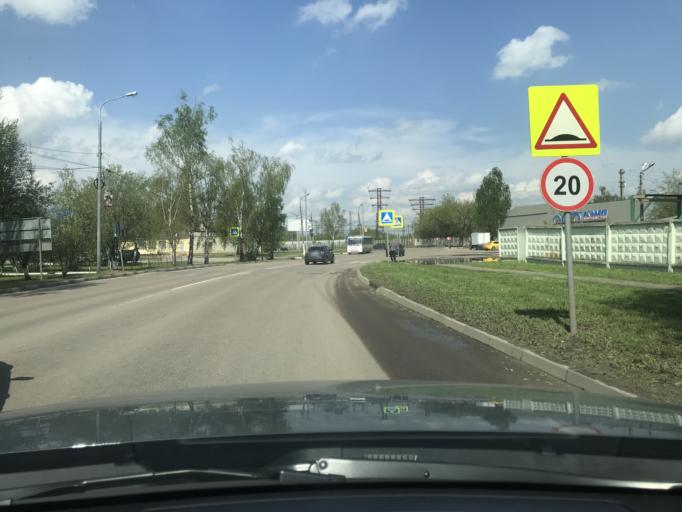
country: RU
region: Moskovskaya
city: Naro-Fominsk
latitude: 55.3811
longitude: 36.7562
